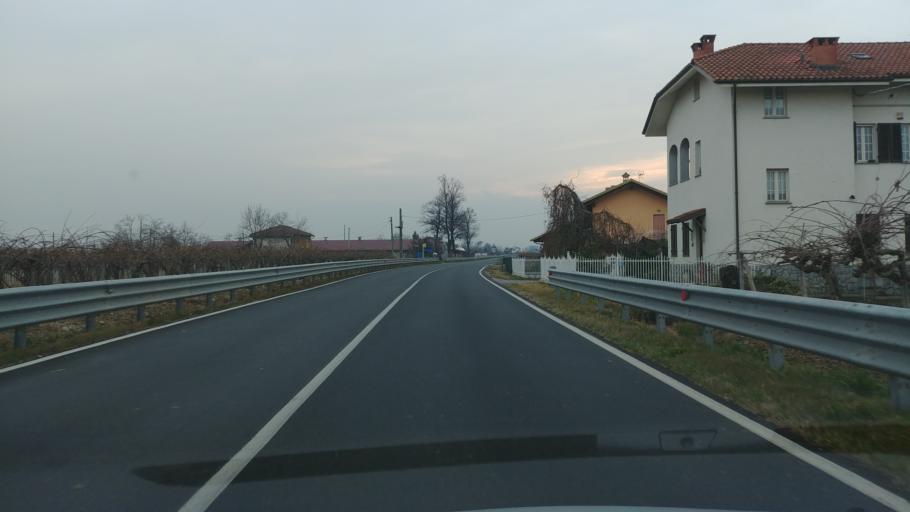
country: IT
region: Piedmont
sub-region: Provincia di Cuneo
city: Montanera
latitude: 44.5027
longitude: 7.6778
